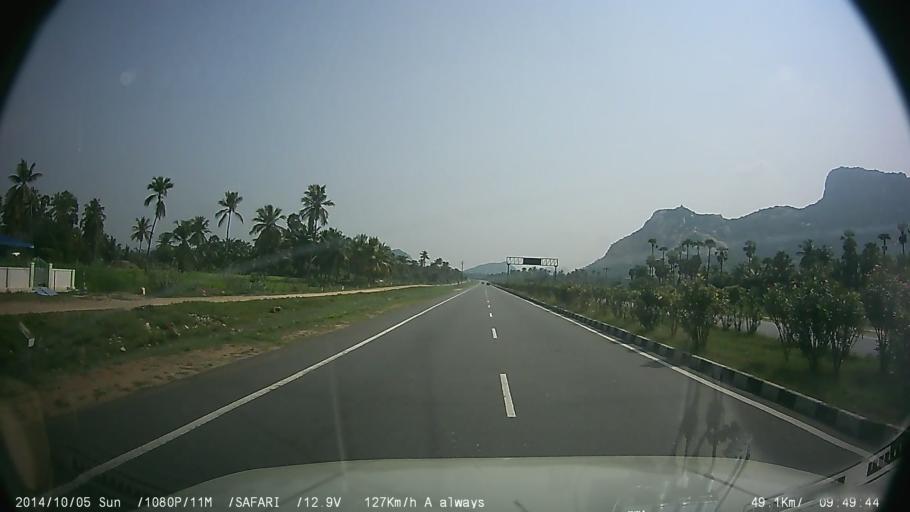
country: IN
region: Tamil Nadu
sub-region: Salem
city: Idappadi
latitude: 11.4810
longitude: 77.8395
